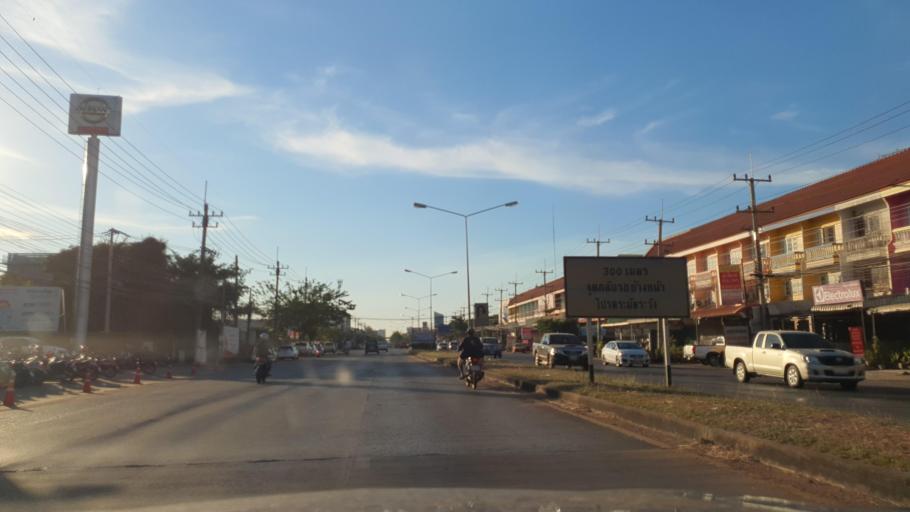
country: TH
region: Khon Kaen
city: Khon Kaen
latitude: 16.4263
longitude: 102.8799
